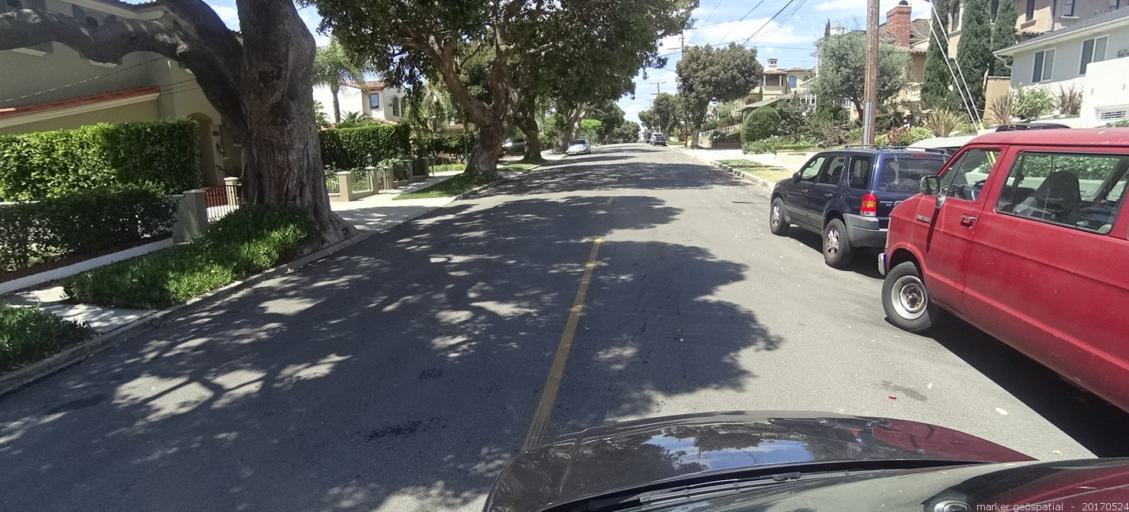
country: US
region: California
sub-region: Los Angeles County
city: Redondo Beach
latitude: 33.8288
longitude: -118.3842
